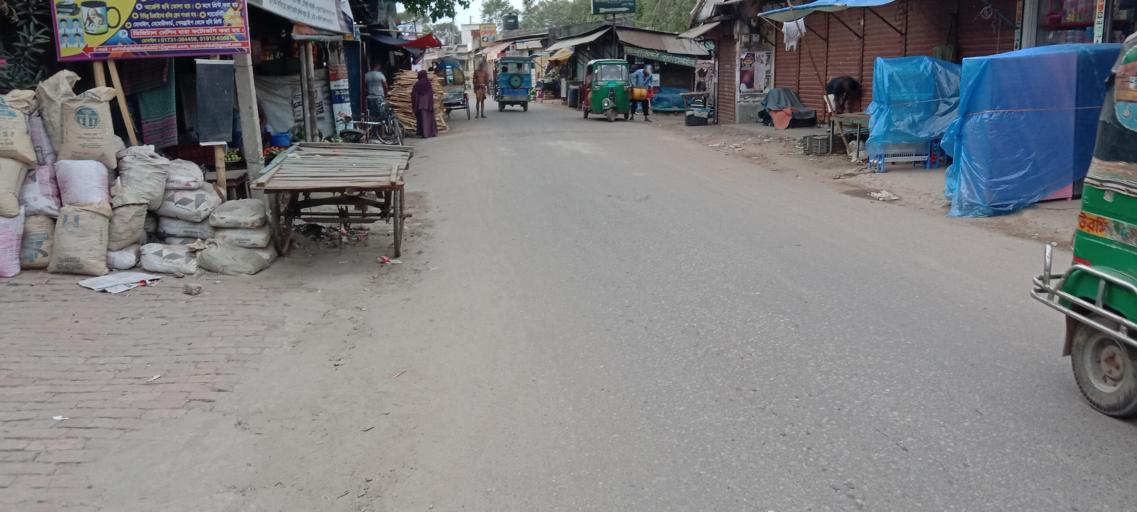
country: BD
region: Dhaka
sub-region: Dhaka
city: Dhaka
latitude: 23.6594
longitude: 90.4145
